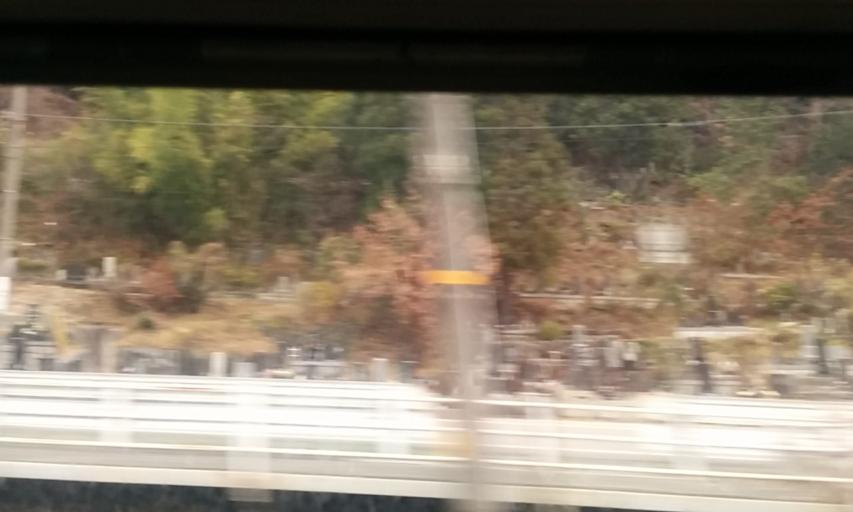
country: JP
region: Nagano
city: Ina
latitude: 35.7895
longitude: 137.6937
